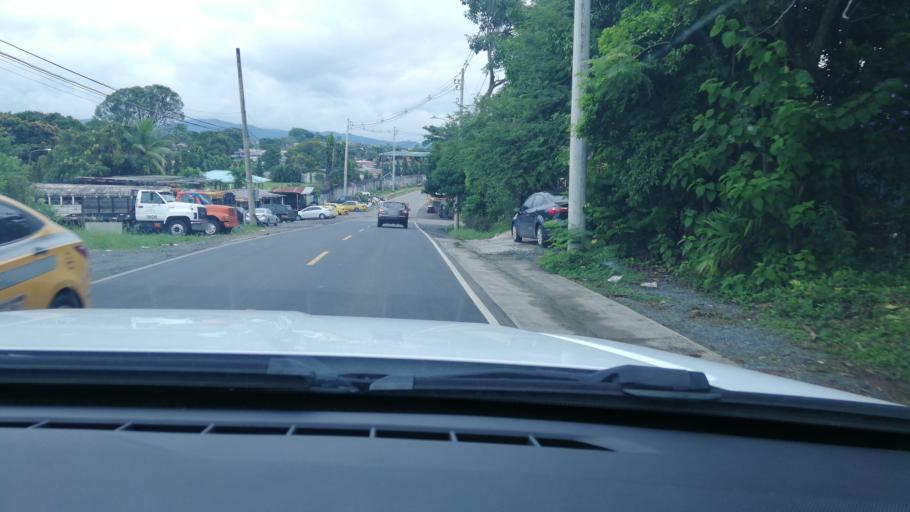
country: PA
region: Panama
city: Las Cumbres
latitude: 9.0746
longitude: -79.5156
